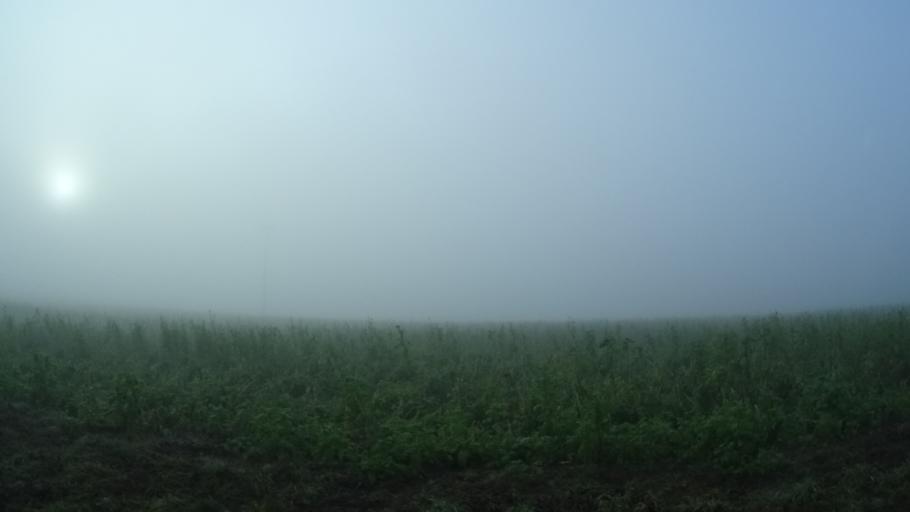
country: DE
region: Bavaria
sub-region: Regierungsbezirk Unterfranken
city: Kreuzwertheim
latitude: 49.7422
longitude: 9.5577
